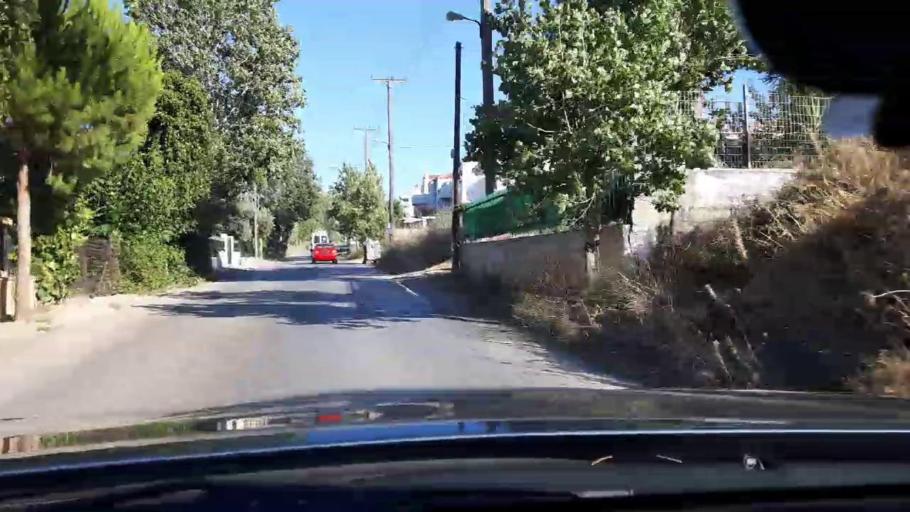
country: GR
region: Attica
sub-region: Nomarchia Anatolikis Attikis
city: Limin Mesoyaias
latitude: 37.8776
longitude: 24.0065
